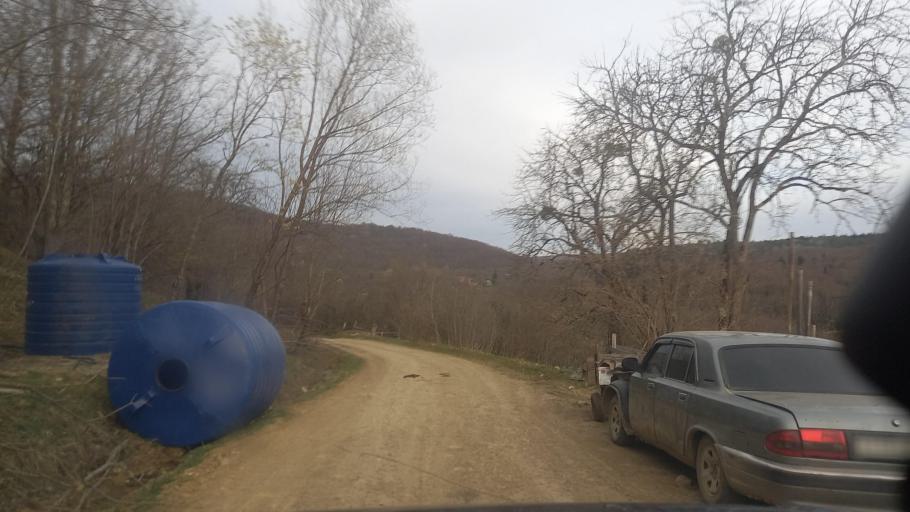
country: RU
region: Adygeya
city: Kamennomostskiy
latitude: 44.2118
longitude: 40.0118
